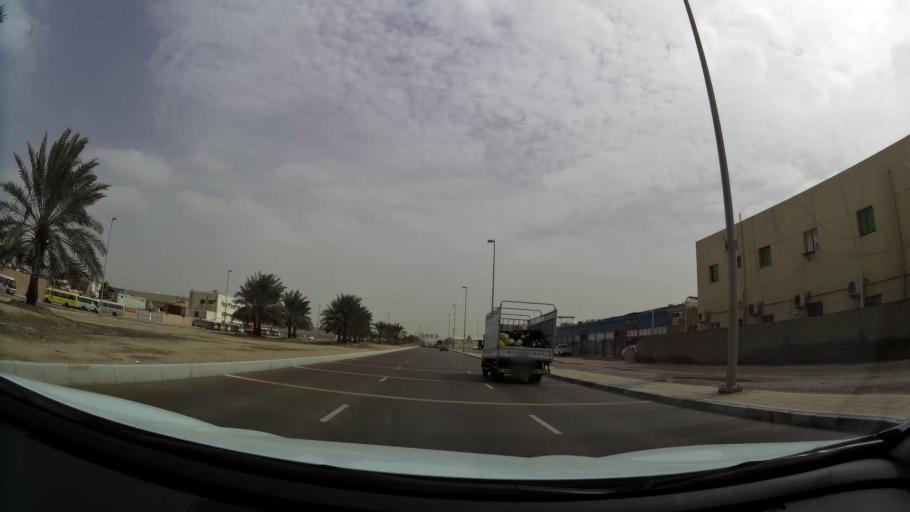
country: AE
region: Abu Dhabi
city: Abu Dhabi
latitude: 24.3722
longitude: 54.4890
